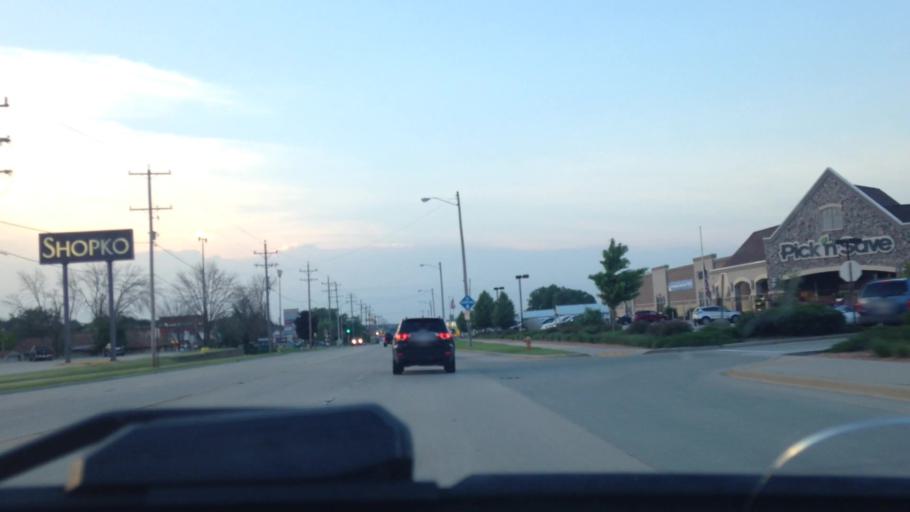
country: US
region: Wisconsin
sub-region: Washington County
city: West Bend
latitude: 43.3992
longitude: -88.1809
